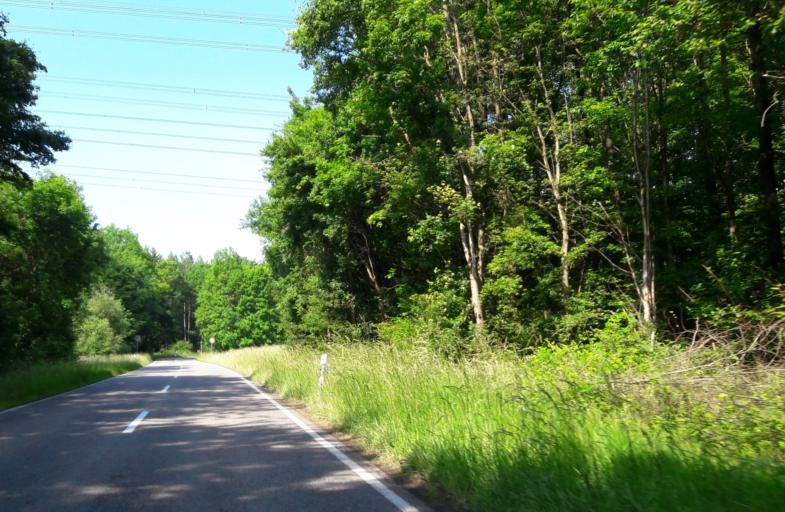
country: DE
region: Saarland
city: Ensdorf
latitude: 49.3161
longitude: 6.7995
